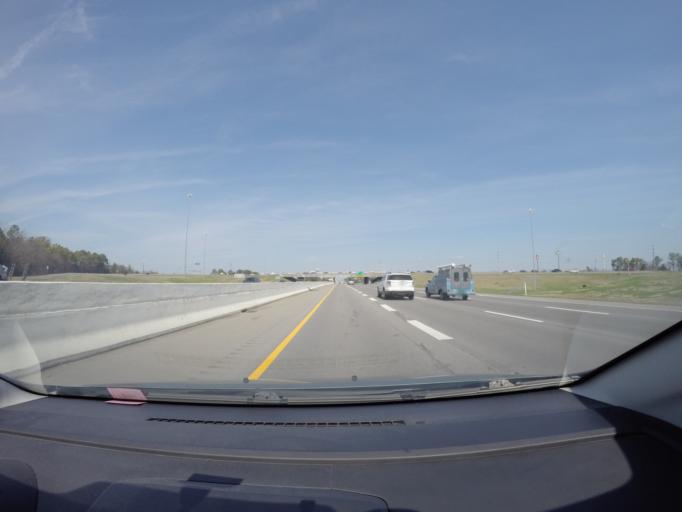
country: US
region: Tennessee
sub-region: Rutherford County
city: Murfreesboro
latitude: 35.8461
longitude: -86.4338
